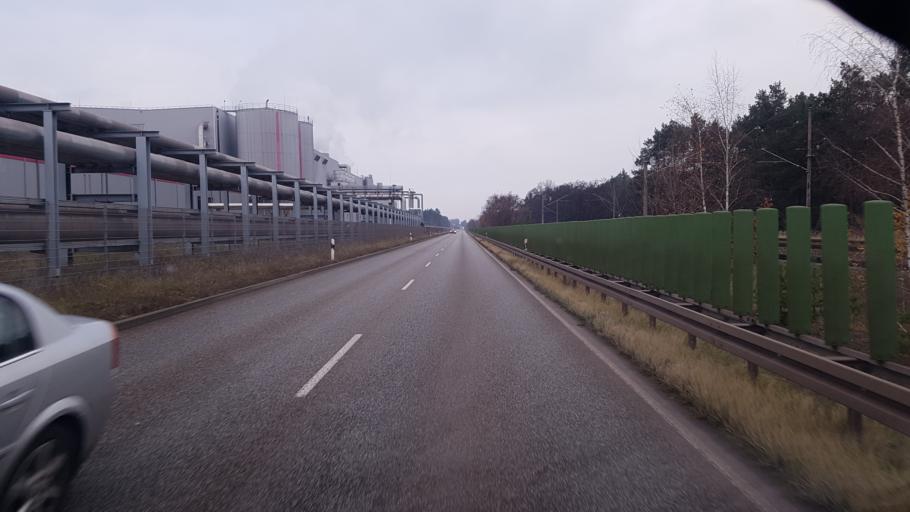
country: DE
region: Brandenburg
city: Vogelsang
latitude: 52.1769
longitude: 14.6387
